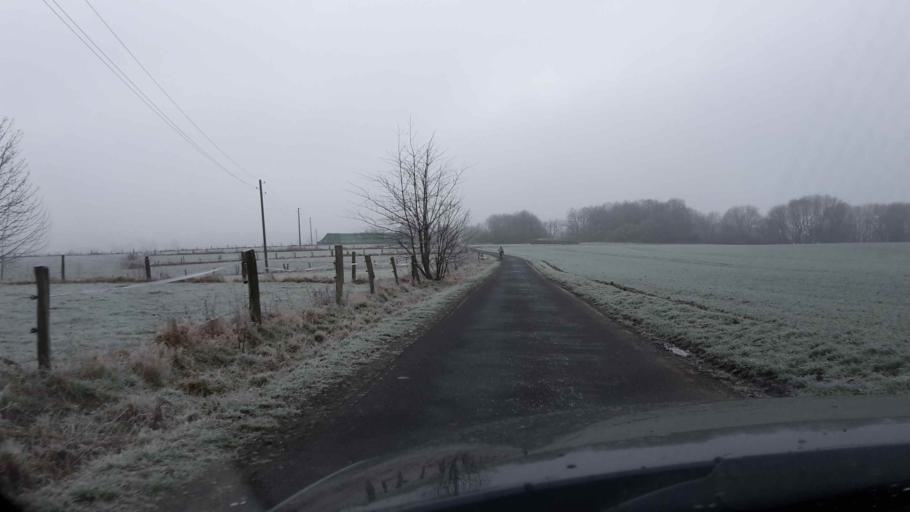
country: DE
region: North Rhine-Westphalia
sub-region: Regierungsbezirk Koln
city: Hennef
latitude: 50.7285
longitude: 7.2931
